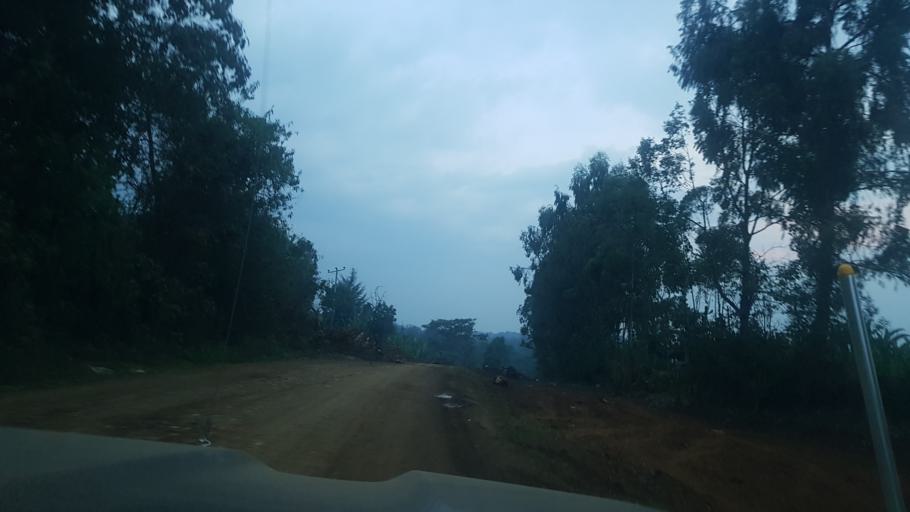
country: ET
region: Oromiya
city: Gore
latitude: 7.7773
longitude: 35.4658
